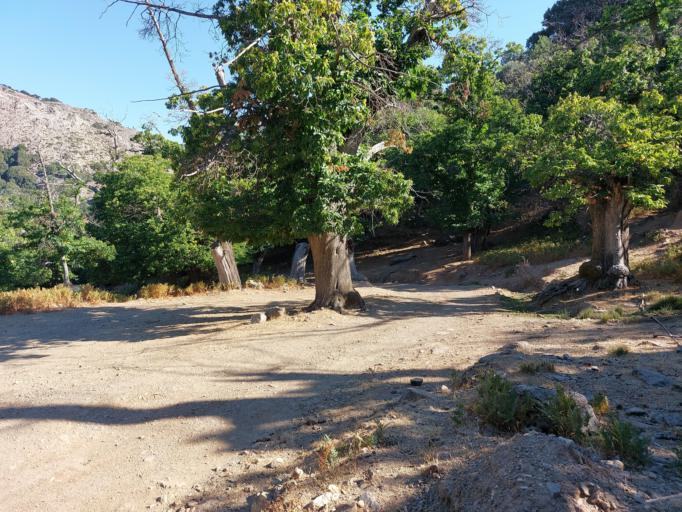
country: GR
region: Crete
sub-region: Nomos Chanias
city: Vryses
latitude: 35.4004
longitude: 23.6255
